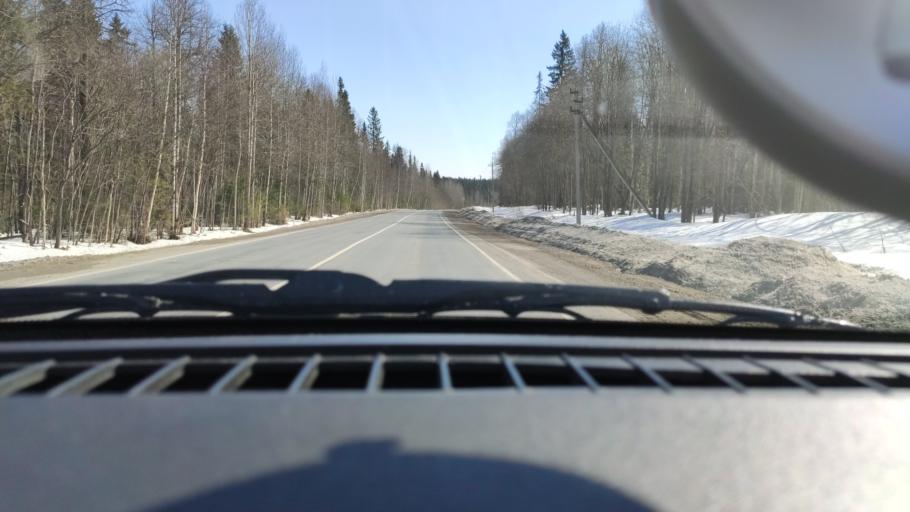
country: RU
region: Perm
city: Perm
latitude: 58.2079
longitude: 56.1939
